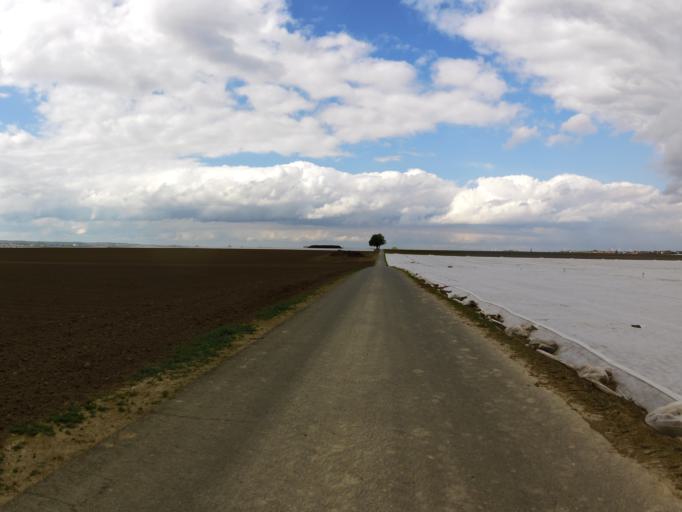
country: DE
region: Bavaria
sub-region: Regierungsbezirk Unterfranken
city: Oberpleichfeld
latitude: 49.8638
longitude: 10.0815
